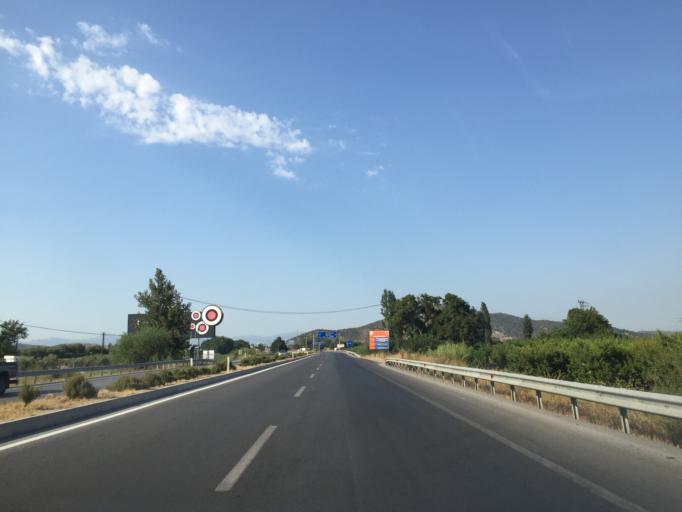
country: TR
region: Izmir
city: Belevi
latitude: 38.0168
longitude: 27.4384
